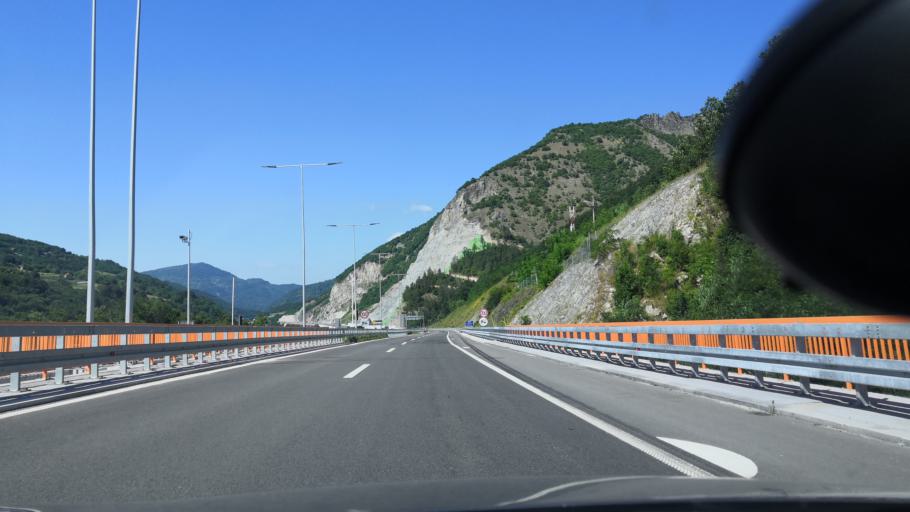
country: RS
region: Central Serbia
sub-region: Pcinjski Okrug
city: Vladicin Han
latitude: 42.7473
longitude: 22.0807
